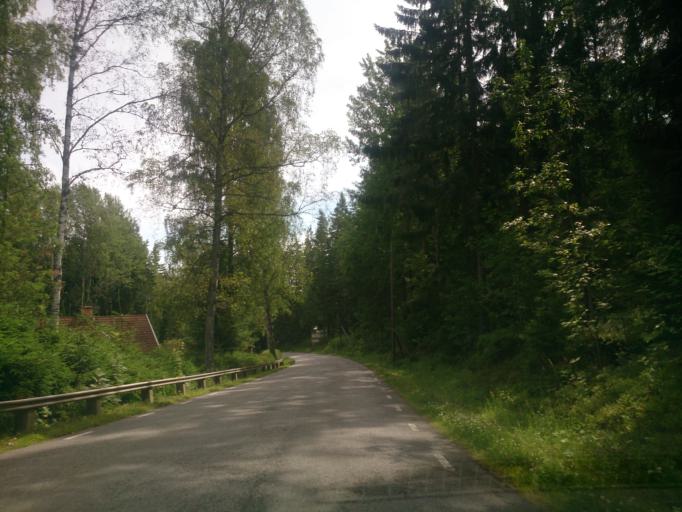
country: SE
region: OEstergoetland
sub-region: Valdemarsviks Kommun
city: Gusum
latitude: 58.3293
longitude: 16.3971
